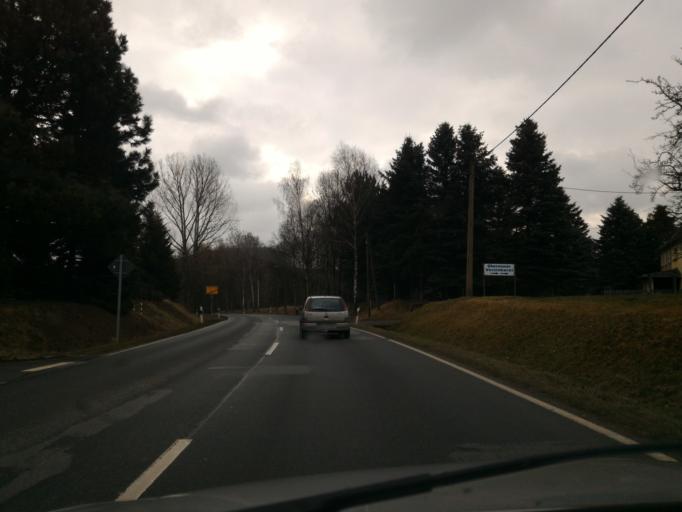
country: DE
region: Saxony
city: Eibau
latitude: 50.9740
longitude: 14.6726
